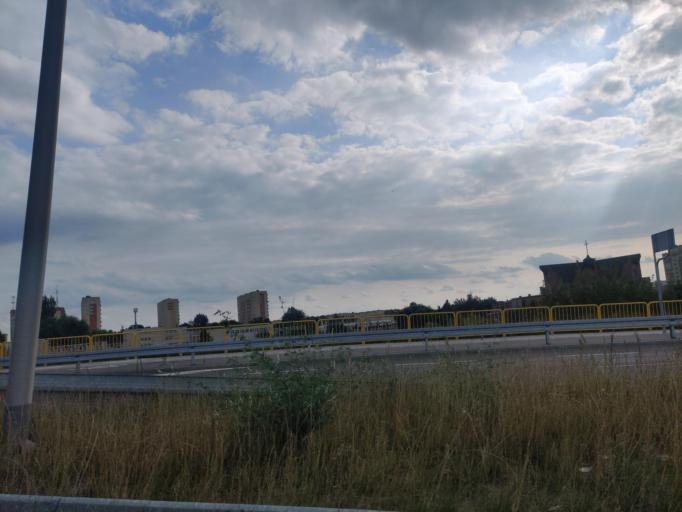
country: PL
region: Greater Poland Voivodeship
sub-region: Konin
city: Konin
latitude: 52.2346
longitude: 18.2719
